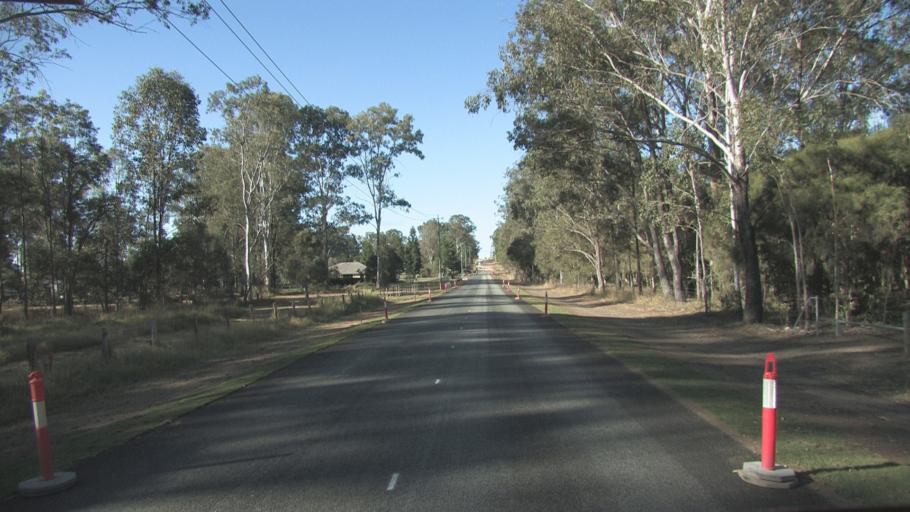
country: AU
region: Queensland
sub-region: Logan
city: Cedar Vale
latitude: -27.8340
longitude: 152.9990
